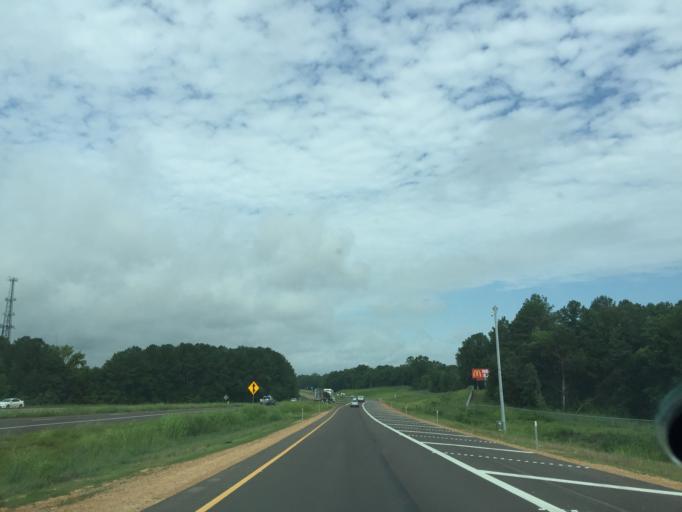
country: US
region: Mississippi
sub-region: Rankin County
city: Brandon
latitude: 32.2790
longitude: -90.0065
